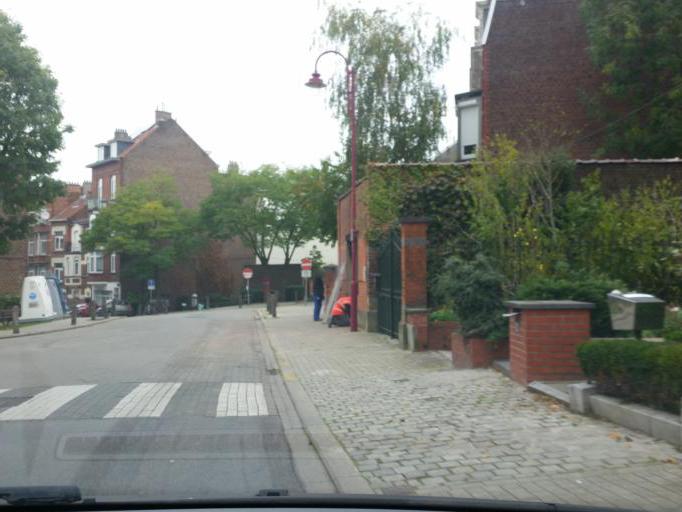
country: BE
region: Flanders
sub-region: Provincie Vlaams-Brabant
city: Drogenbos
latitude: 50.8076
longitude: 4.3191
